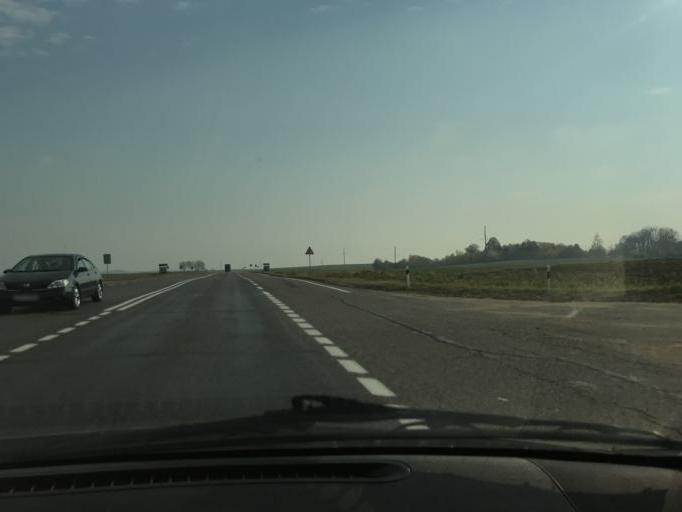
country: BY
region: Vitebsk
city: Chashniki
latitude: 55.0159
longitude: 29.0457
